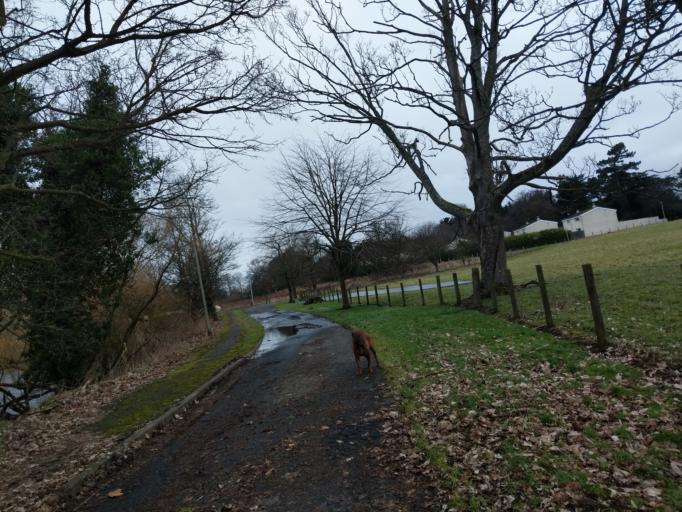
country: GB
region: Scotland
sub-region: Edinburgh
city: Ratho
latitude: 55.9633
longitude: -3.3317
